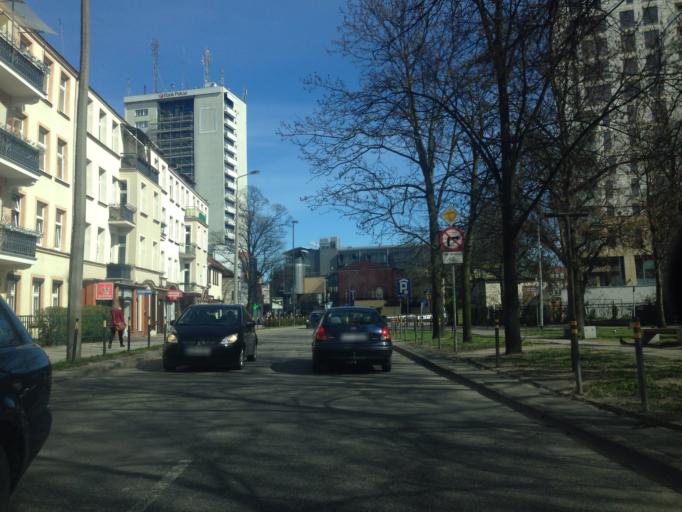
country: PL
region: Pomeranian Voivodeship
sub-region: Gdansk
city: Gdansk
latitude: 54.3780
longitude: 18.6040
